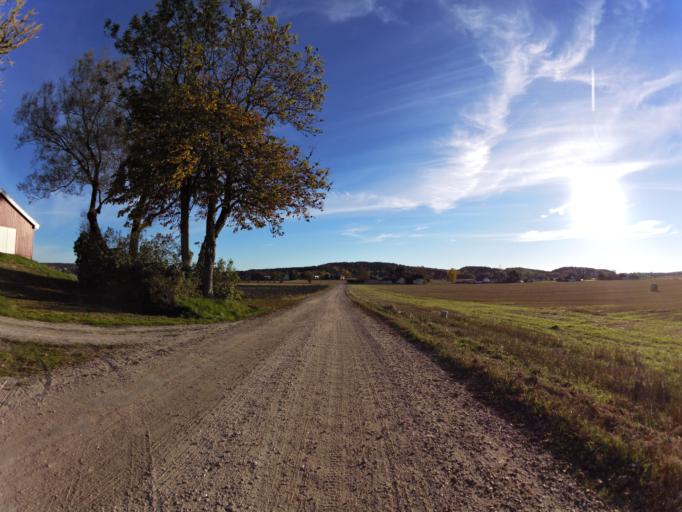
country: NO
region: Ostfold
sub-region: Sarpsborg
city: Sarpsborg
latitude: 59.2621
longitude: 11.0715
